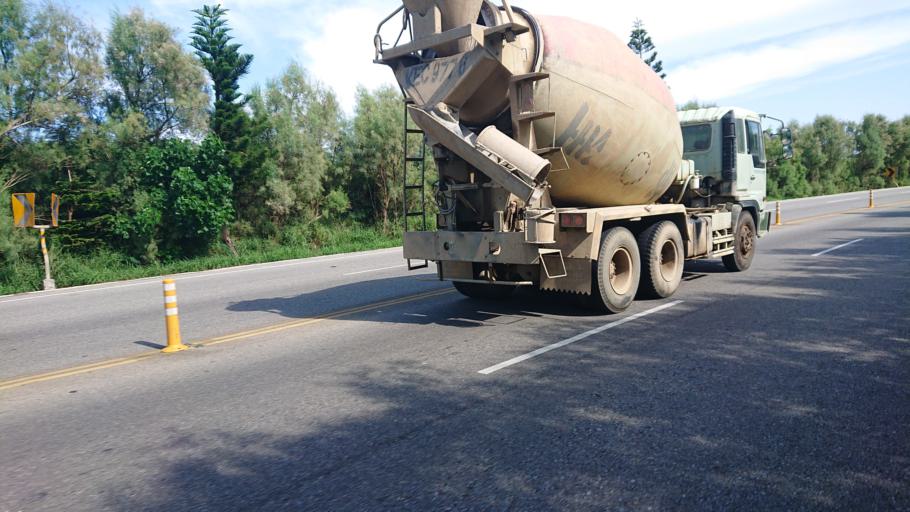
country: TW
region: Taiwan
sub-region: Penghu
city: Ma-kung
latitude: 23.5419
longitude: 119.6062
